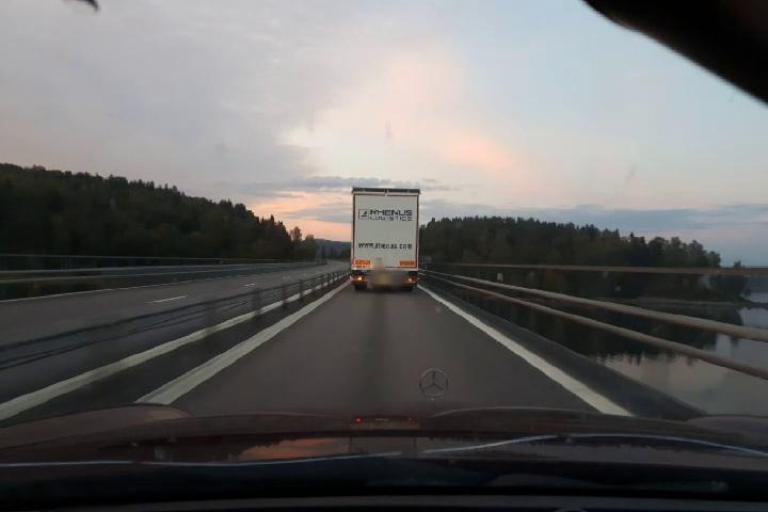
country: SE
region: Vaesternorrland
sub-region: Haernoesands Kommun
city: Haernoesand
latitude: 62.8207
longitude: 17.9701
